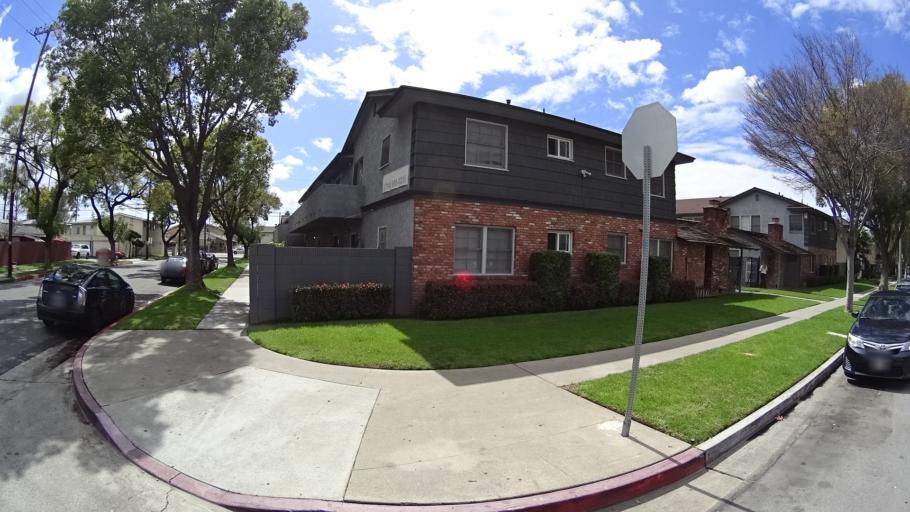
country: US
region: California
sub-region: Orange County
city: Anaheim
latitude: 33.8189
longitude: -117.9372
